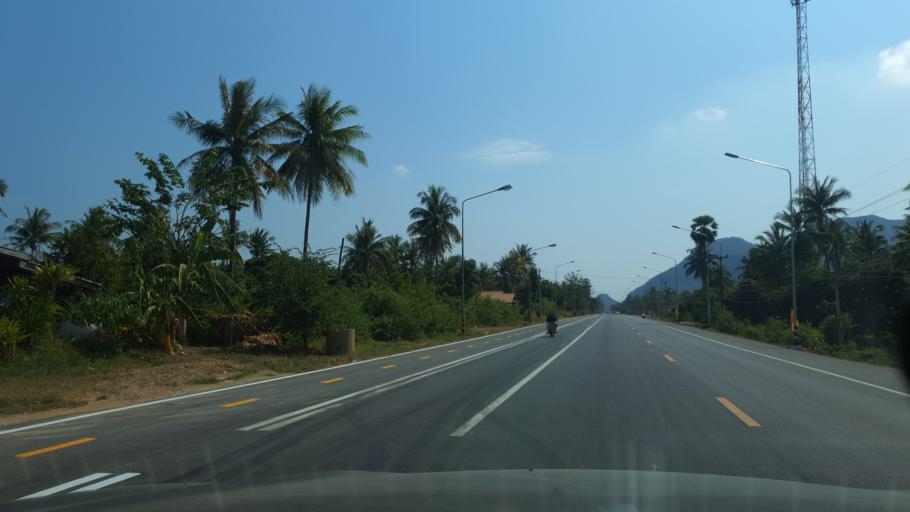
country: TH
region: Prachuap Khiri Khan
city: Sam Roi Yot
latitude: 12.2437
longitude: 99.9645
